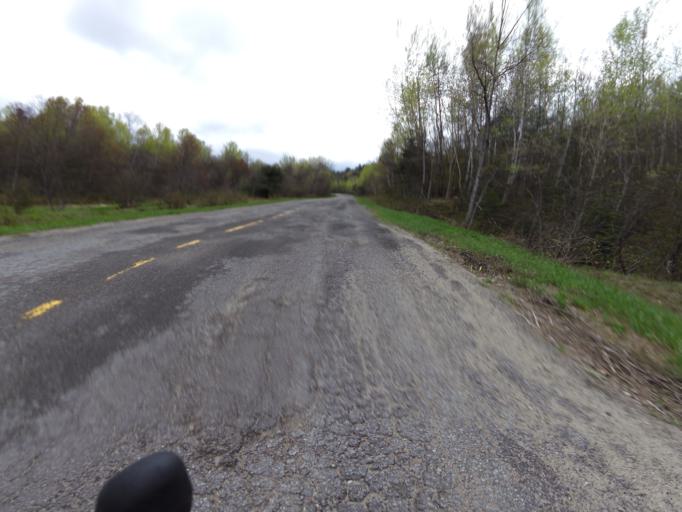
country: CA
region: Quebec
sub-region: Outaouais
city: Wakefield
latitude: 45.6079
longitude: -75.8624
